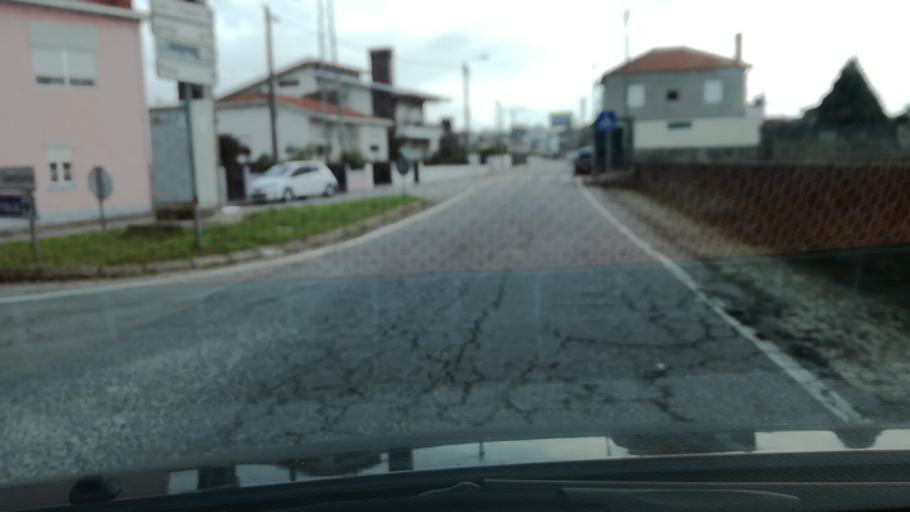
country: PT
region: Porto
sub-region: Maia
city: Gemunde
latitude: 41.2676
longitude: -8.6521
